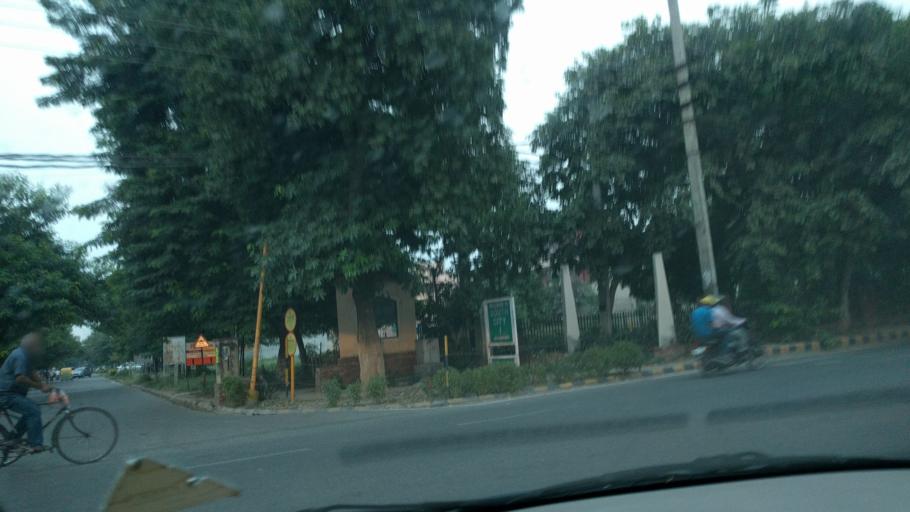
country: IN
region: Haryana
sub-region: Gurgaon
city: Gurgaon
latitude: 28.4521
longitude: 77.0607
